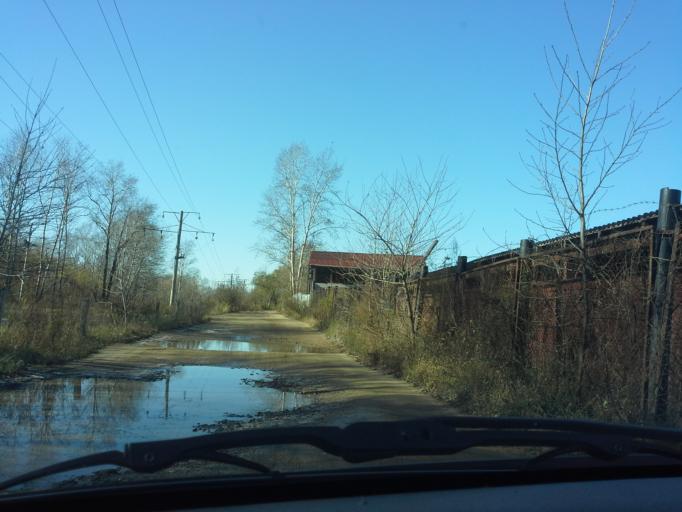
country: RU
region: Jewish Autonomous Oblast
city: Priamurskiy
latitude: 48.5325
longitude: 134.9654
